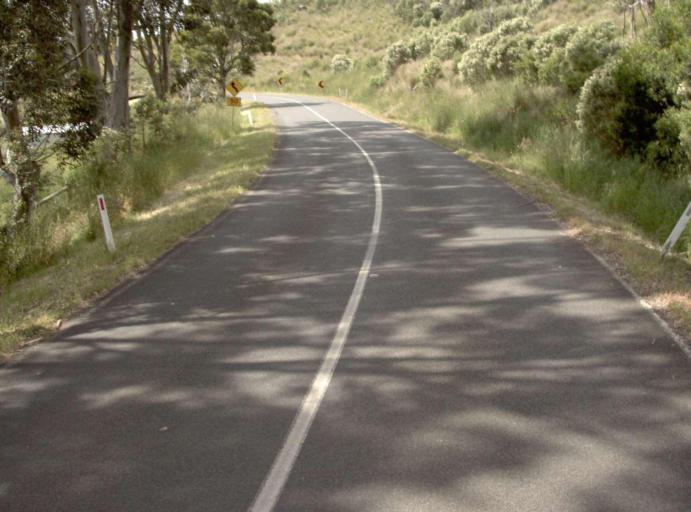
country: AU
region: Victoria
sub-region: Latrobe
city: Traralgon
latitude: -38.3501
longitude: 146.5687
